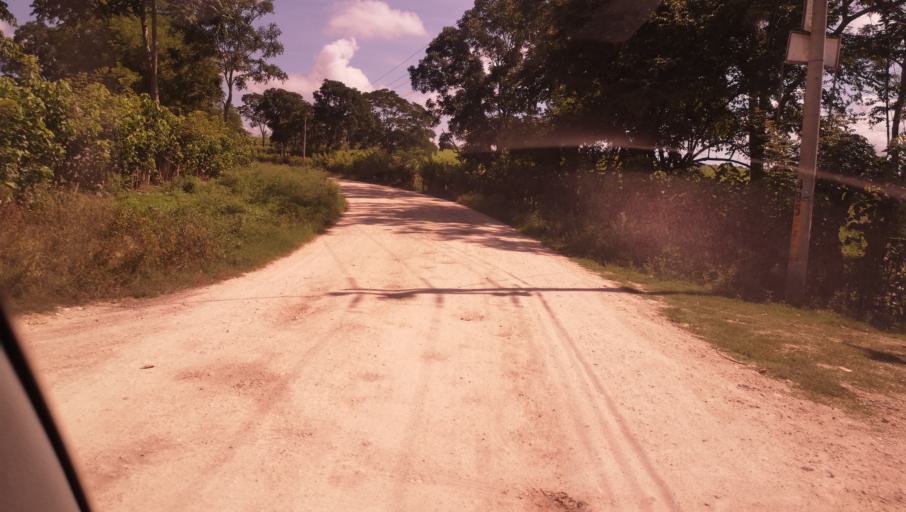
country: GT
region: Peten
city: Melchor de Mencos
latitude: 16.8408
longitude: -89.2987
